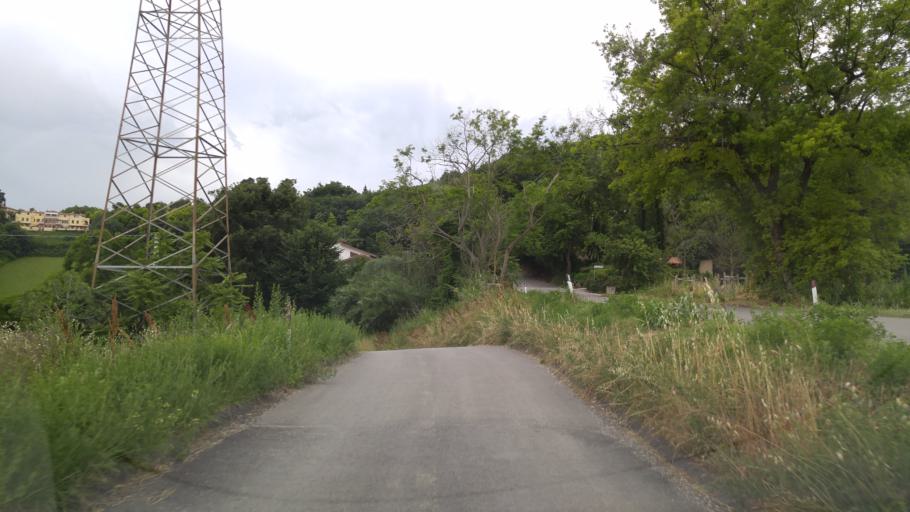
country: IT
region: The Marches
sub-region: Provincia di Pesaro e Urbino
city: Fenile
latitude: 43.8634
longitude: 12.9340
